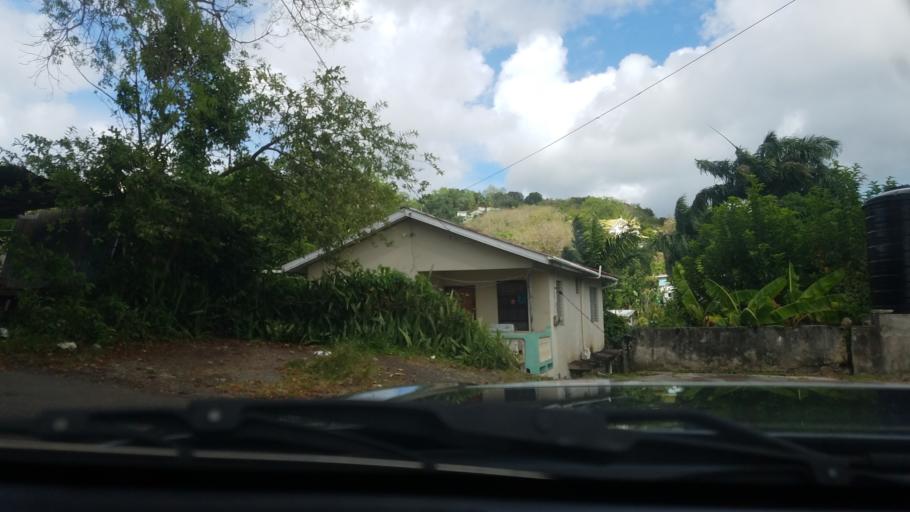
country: LC
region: Castries Quarter
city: Bisee
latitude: 14.0089
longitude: -60.9848
